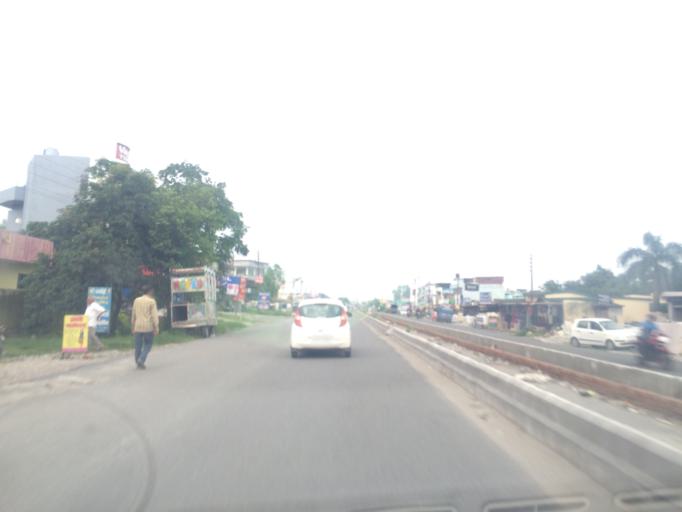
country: IN
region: Uttarakhand
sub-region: Dehradun
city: Doiwala
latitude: 30.1866
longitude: 78.1494
